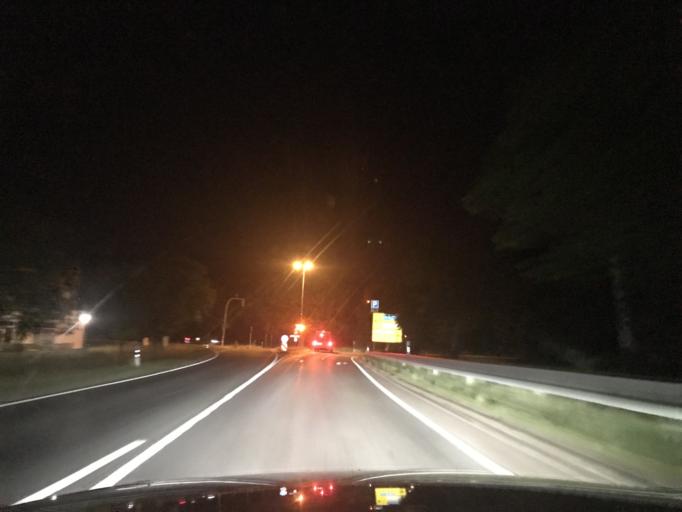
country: DE
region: Bavaria
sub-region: Upper Franconia
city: Ebermannstadt
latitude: 49.7836
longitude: 11.1900
